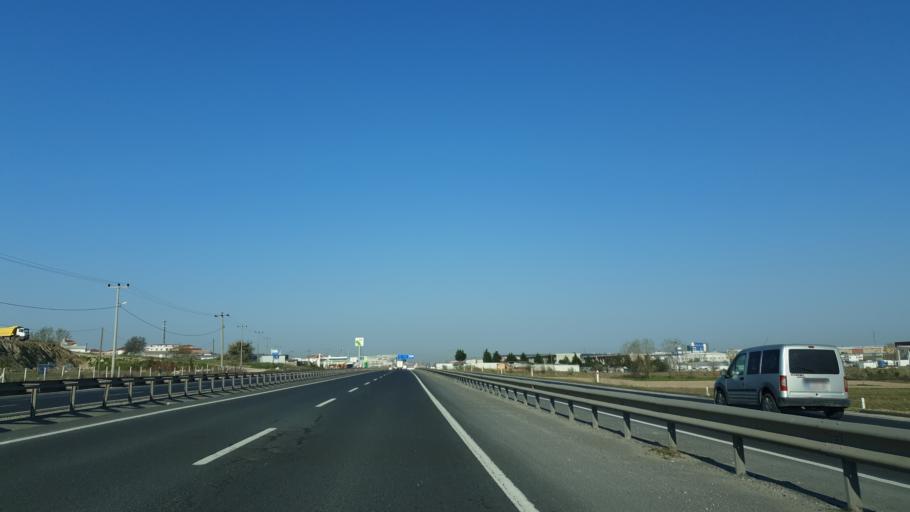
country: TR
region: Tekirdag
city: Cerkezkoey
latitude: 41.2651
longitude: 27.9487
